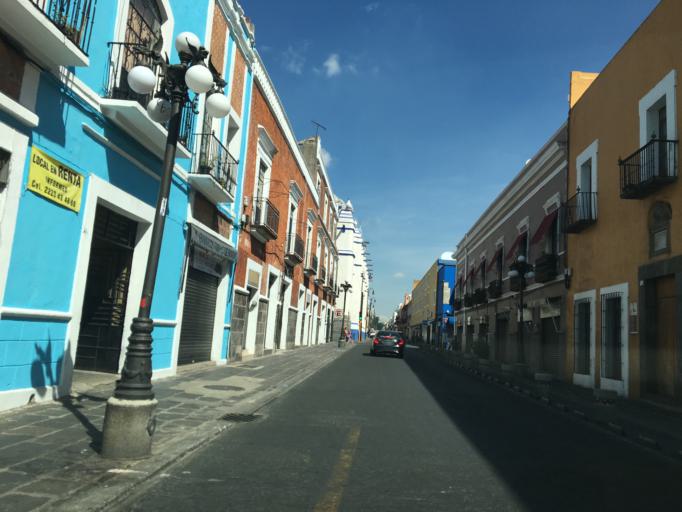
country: MX
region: Puebla
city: Puebla
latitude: 19.0419
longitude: -98.1995
